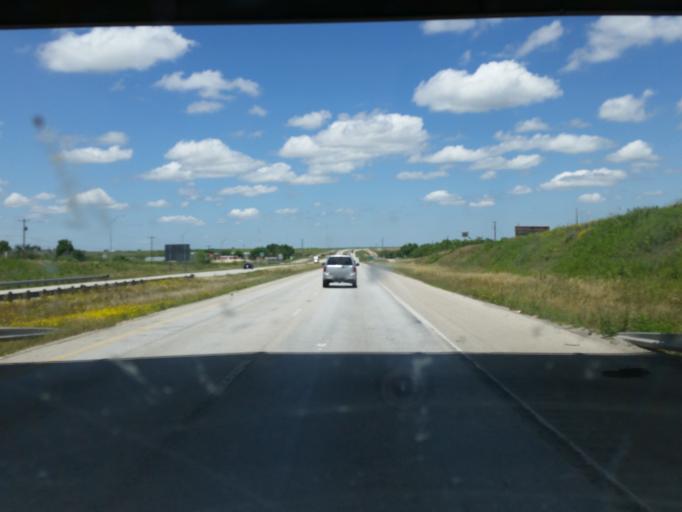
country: US
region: Texas
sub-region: Nolan County
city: Sweetwater
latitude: 32.4548
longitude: -100.3895
